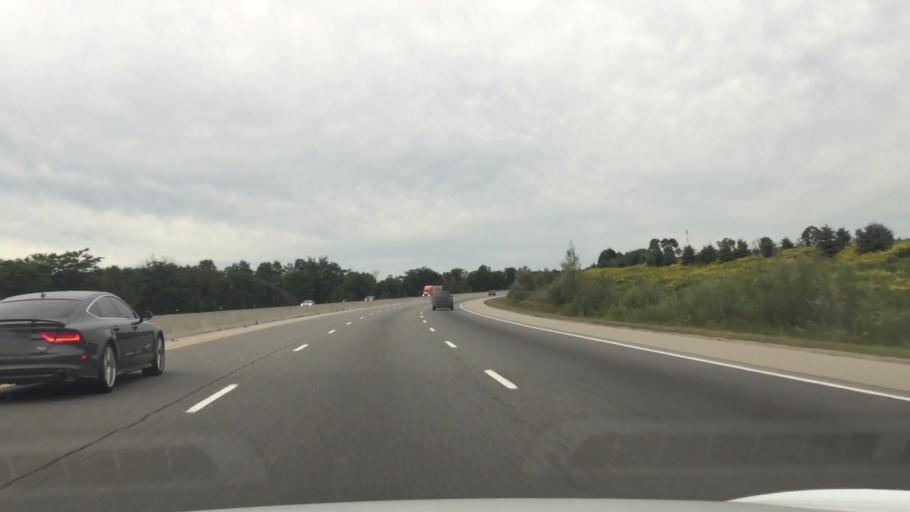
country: CA
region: Ontario
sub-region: Oxford County
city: Woodstock
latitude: 43.2125
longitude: -80.6087
